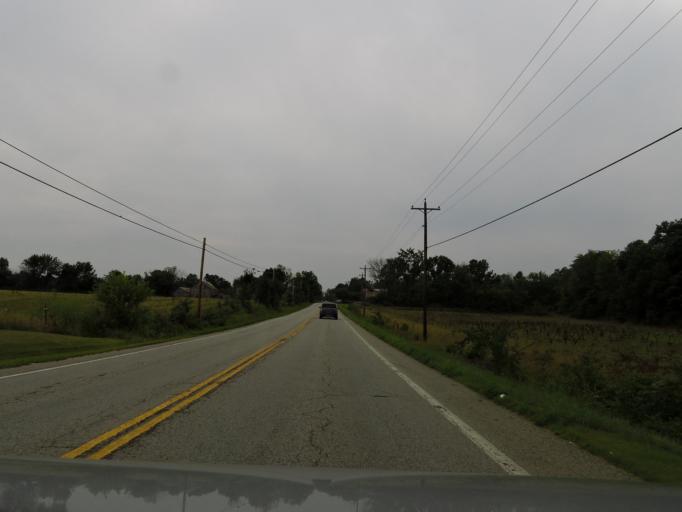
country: US
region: Ohio
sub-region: Brown County
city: Mount Orab
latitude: 39.0606
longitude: -83.9245
